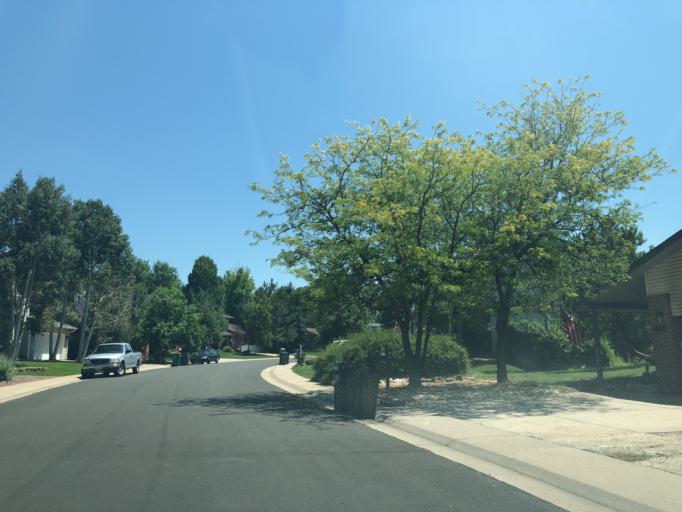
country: US
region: Colorado
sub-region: Arapahoe County
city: Dove Valley
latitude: 39.6232
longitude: -104.7793
